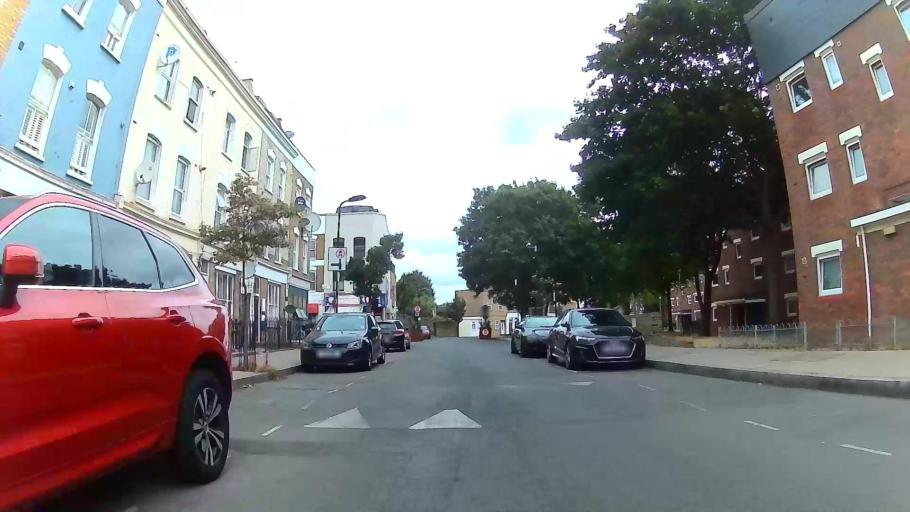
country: GB
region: England
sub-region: Greater London
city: Hackney
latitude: 51.5573
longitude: -0.0789
